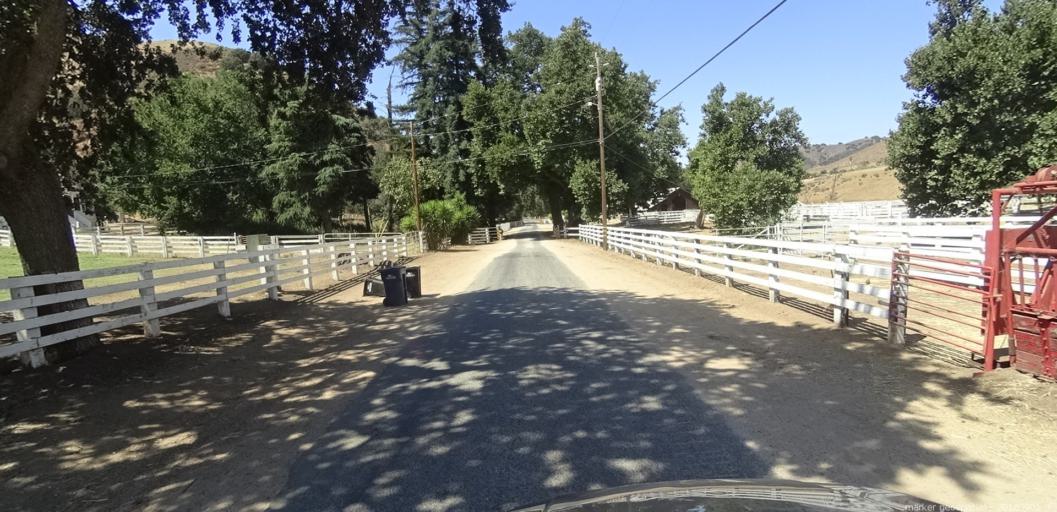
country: US
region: California
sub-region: Monterey County
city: Gonzales
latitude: 36.6035
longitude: -121.4120
